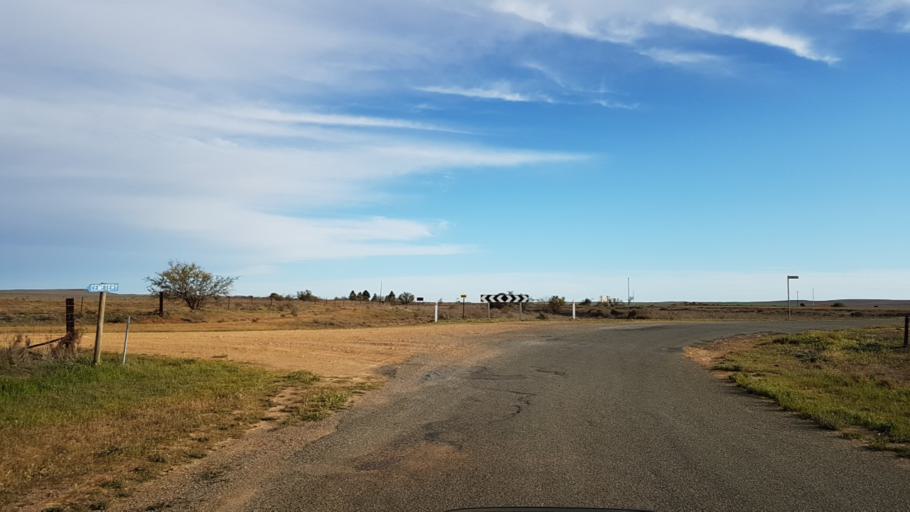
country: AU
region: South Australia
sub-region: Peterborough
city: Peterborough
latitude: -32.9896
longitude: 138.8493
